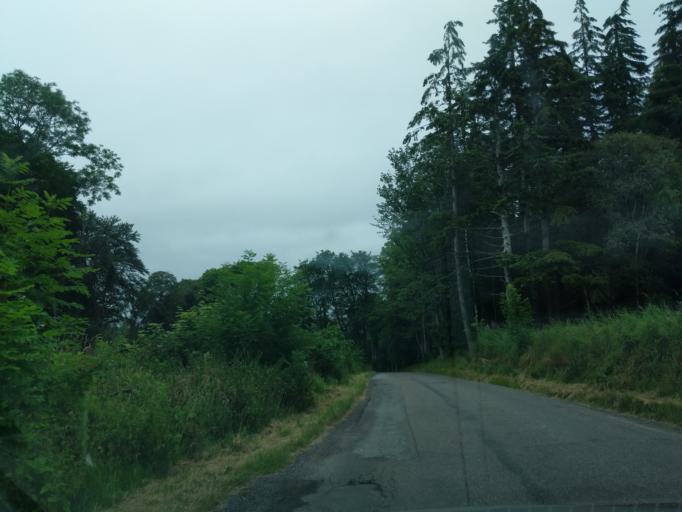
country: GB
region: Scotland
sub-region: Moray
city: Rothes
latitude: 57.4768
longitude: -3.1971
